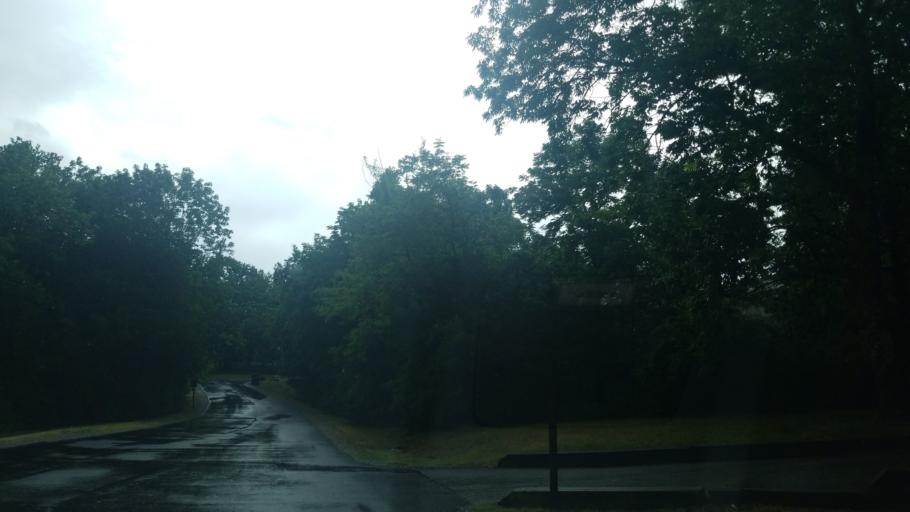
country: US
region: Tennessee
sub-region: Rutherford County
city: La Vergne
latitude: 36.1057
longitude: -86.6040
